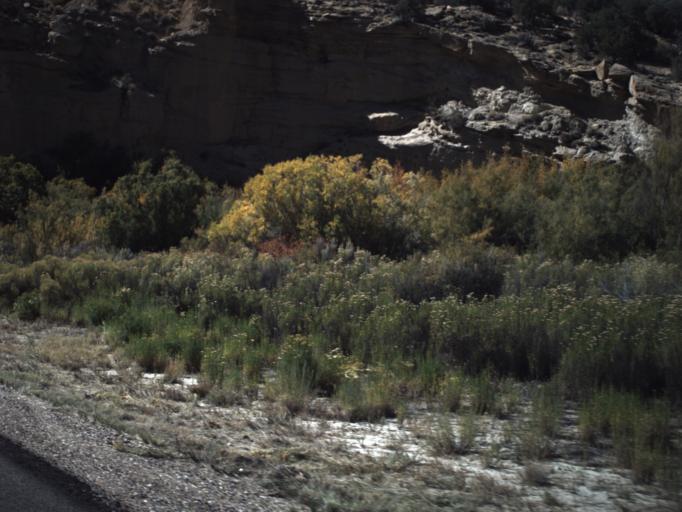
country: US
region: Utah
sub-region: Garfield County
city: Panguitch
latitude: 37.6032
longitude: -111.9158
